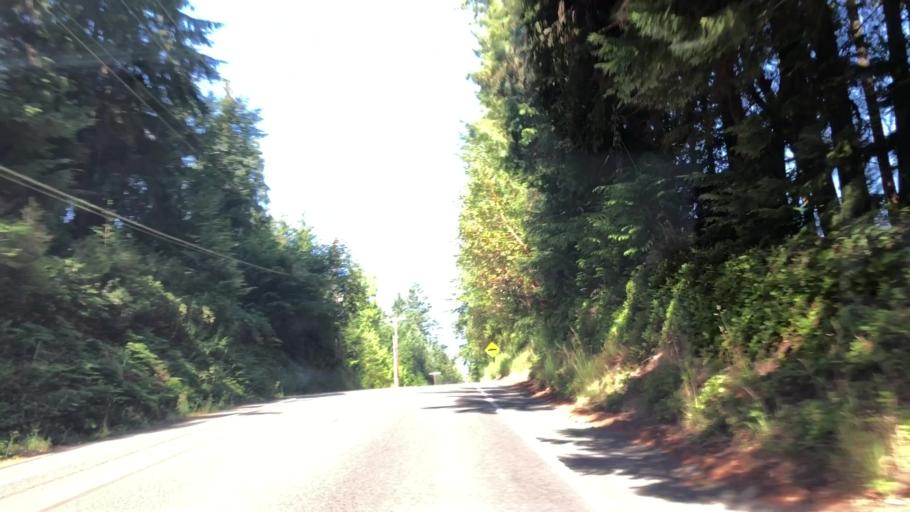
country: US
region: Washington
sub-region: Kitsap County
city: Kingston
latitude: 47.7729
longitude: -122.5054
